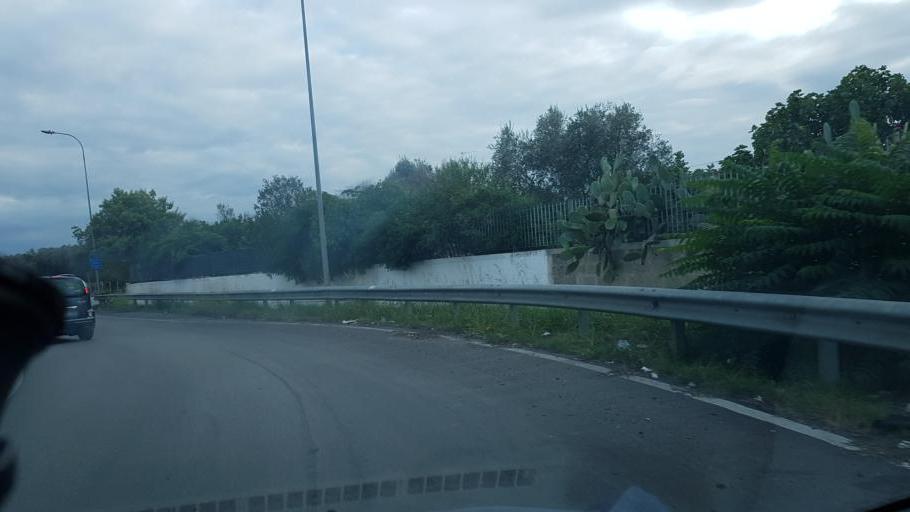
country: IT
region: Apulia
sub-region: Provincia di Brindisi
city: Oria
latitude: 40.5054
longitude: 17.6299
